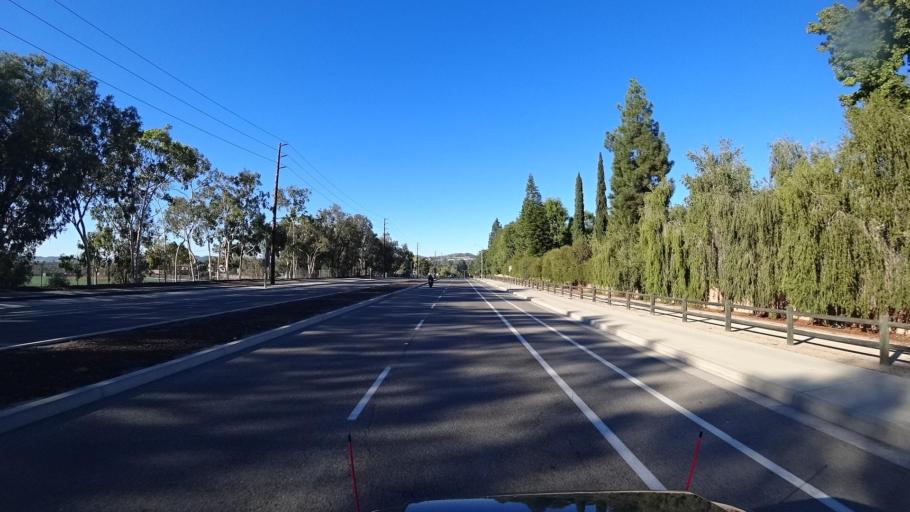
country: US
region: California
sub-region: Orange County
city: Laguna Hills
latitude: 33.5942
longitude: -117.7049
